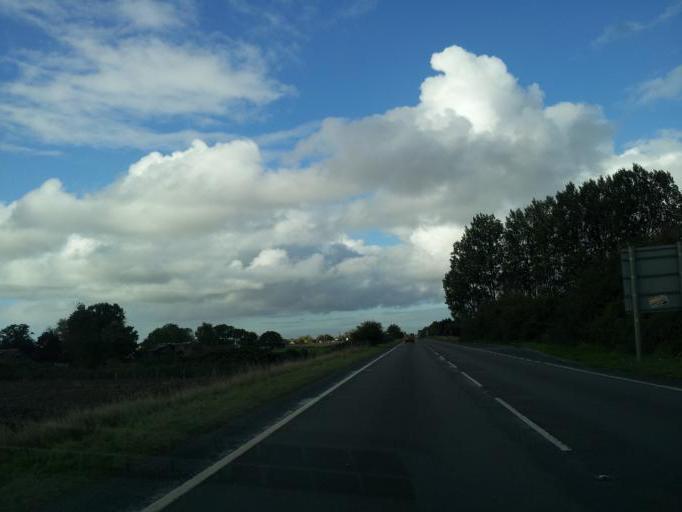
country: GB
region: England
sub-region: Norfolk
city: Terrington St Clement
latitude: 52.7466
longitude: 0.2792
